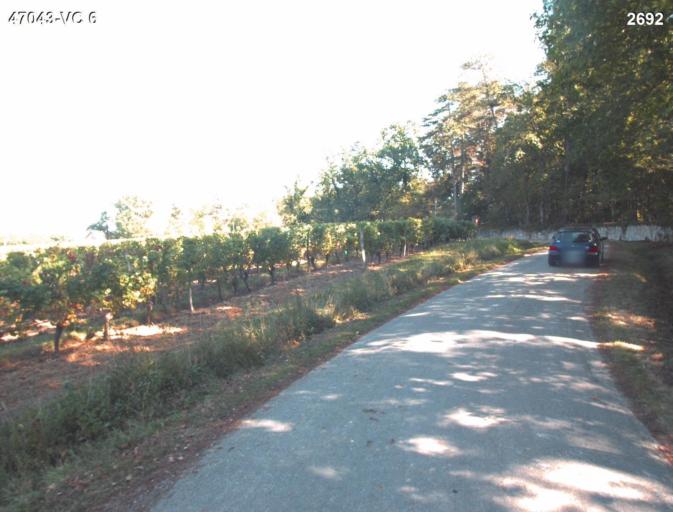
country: FR
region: Aquitaine
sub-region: Departement du Lot-et-Garonne
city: Buzet-sur-Baise
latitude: 44.2314
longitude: 0.2899
